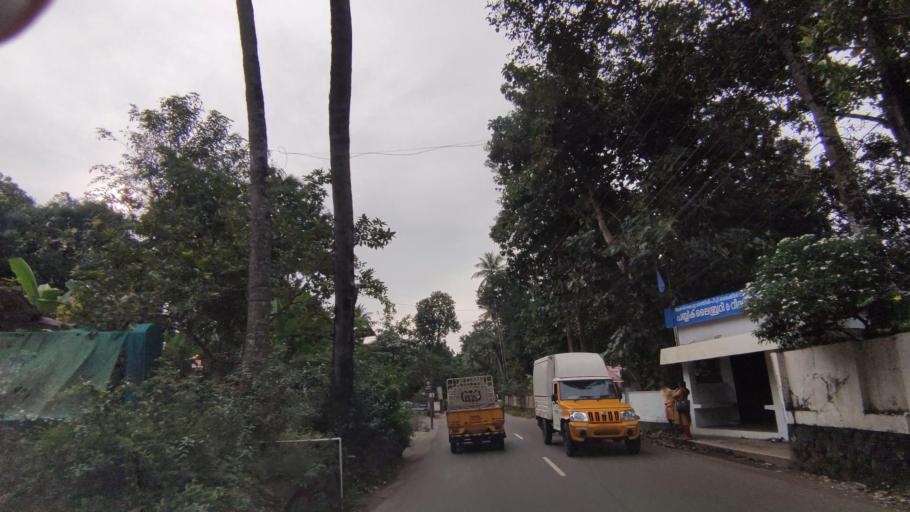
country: IN
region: Kerala
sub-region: Kottayam
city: Kottayam
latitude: 9.6864
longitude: 76.5047
